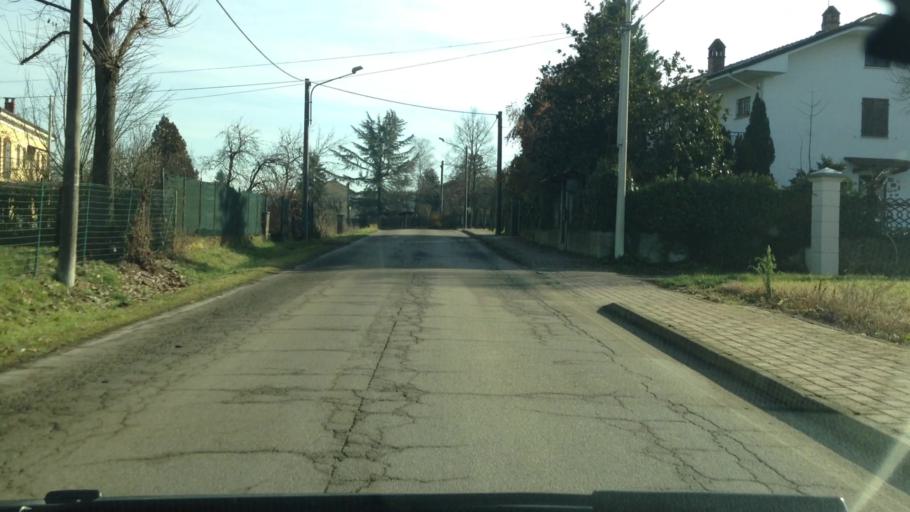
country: IT
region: Piedmont
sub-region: Provincia di Alessandria
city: Masio
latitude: 44.8706
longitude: 8.4135
